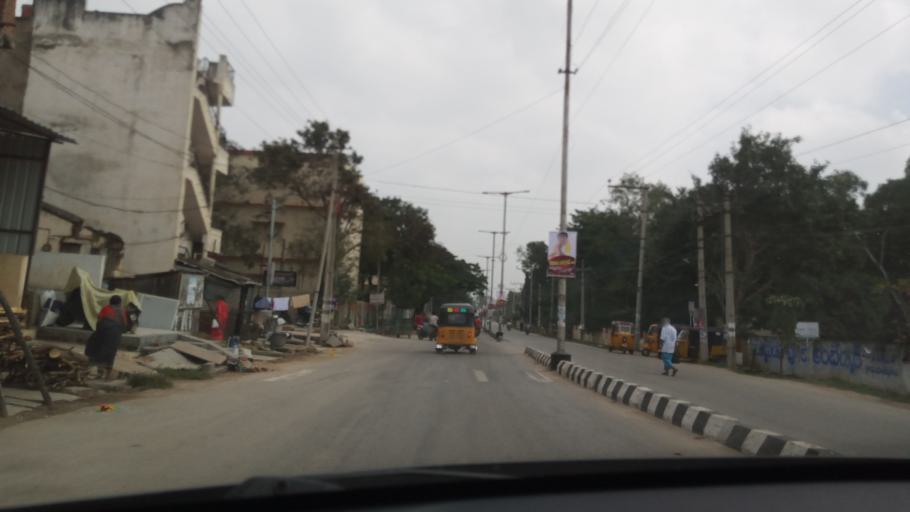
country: IN
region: Andhra Pradesh
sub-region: Chittoor
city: Madanapalle
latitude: 13.5560
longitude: 78.4961
